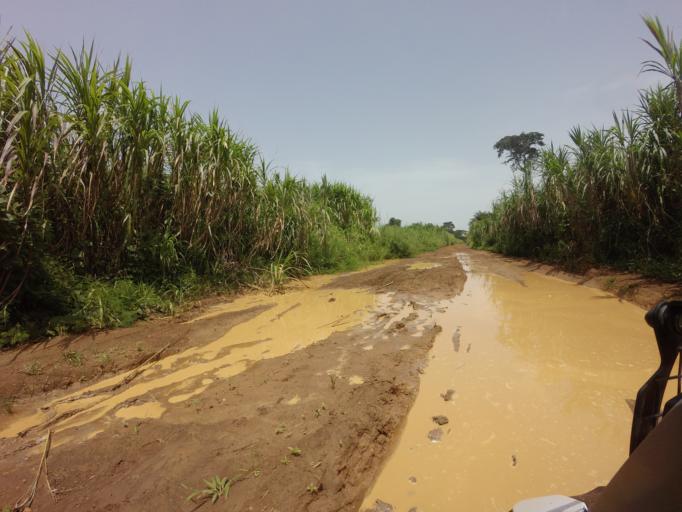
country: GN
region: Nzerekore
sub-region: Lola
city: Lola
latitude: 7.7274
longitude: -8.4021
